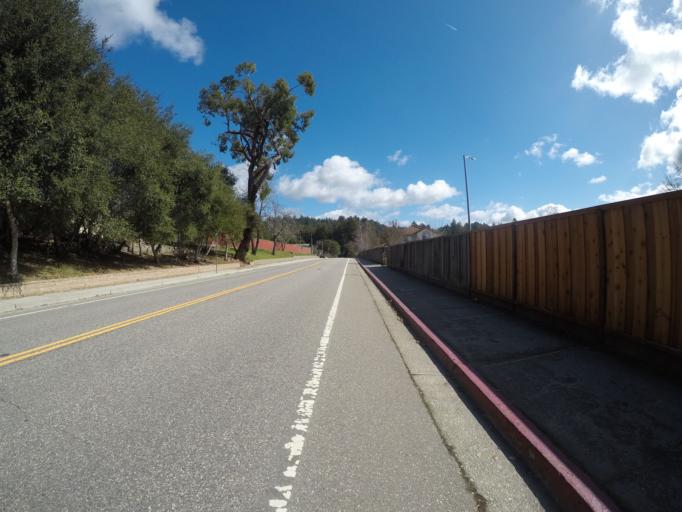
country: US
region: California
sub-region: Santa Cruz County
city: Scotts Valley
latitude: 37.0674
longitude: -122.0005
